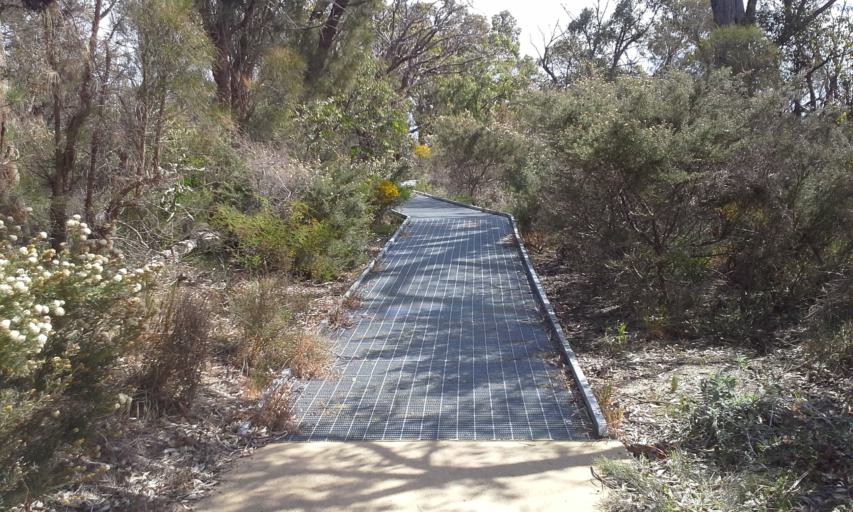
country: AU
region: Western Australia
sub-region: City of Perth
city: West Perth
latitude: -31.9634
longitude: 115.8365
